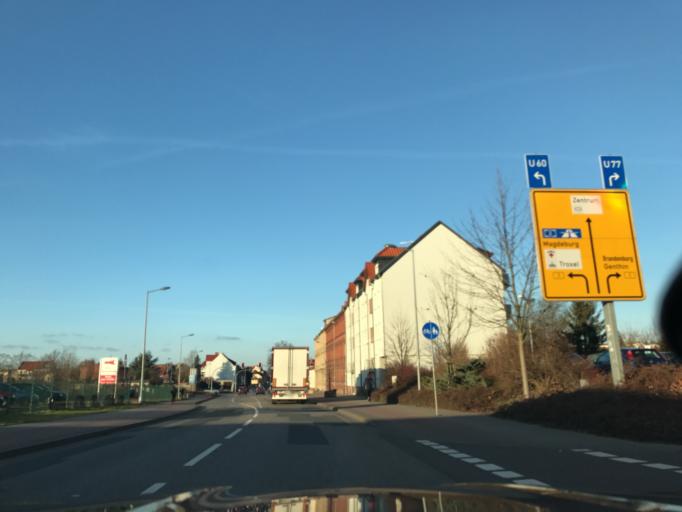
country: DE
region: Saxony-Anhalt
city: Burg bei Magdeburg
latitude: 52.2645
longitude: 11.8624
